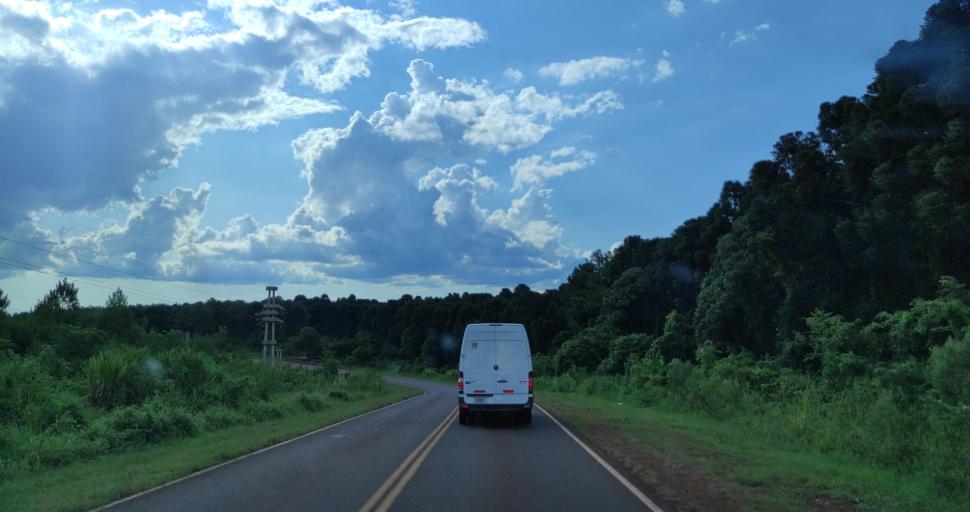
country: AR
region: Misiones
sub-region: Departamento de San Pedro
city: San Pedro
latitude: -26.3474
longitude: -53.9845
